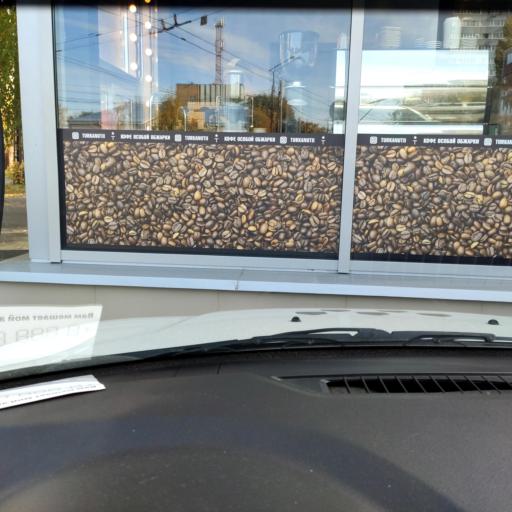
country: RU
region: Samara
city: Tol'yatti
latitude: 53.5219
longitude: 49.4209
